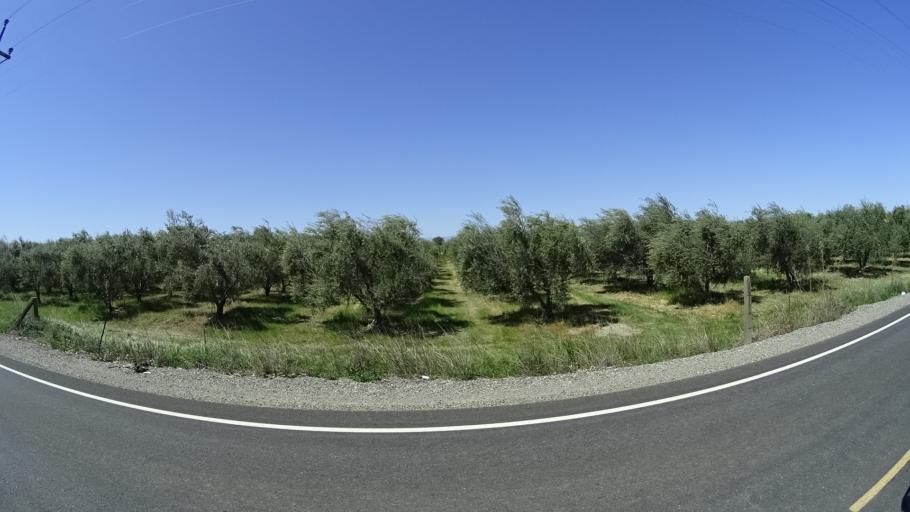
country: US
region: California
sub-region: Glenn County
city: Orland
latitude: 39.7558
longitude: -122.1410
